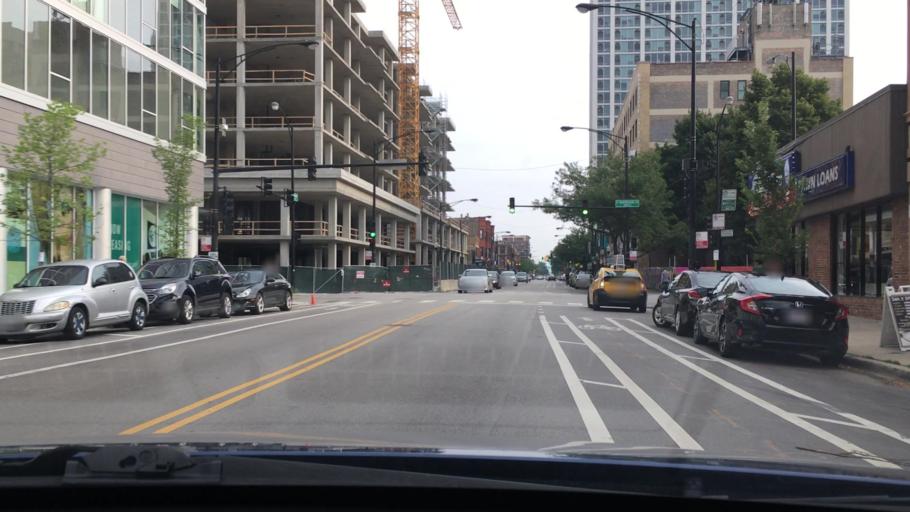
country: US
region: Illinois
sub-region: Cook County
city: Lincolnwood
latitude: 41.9532
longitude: -87.6497
